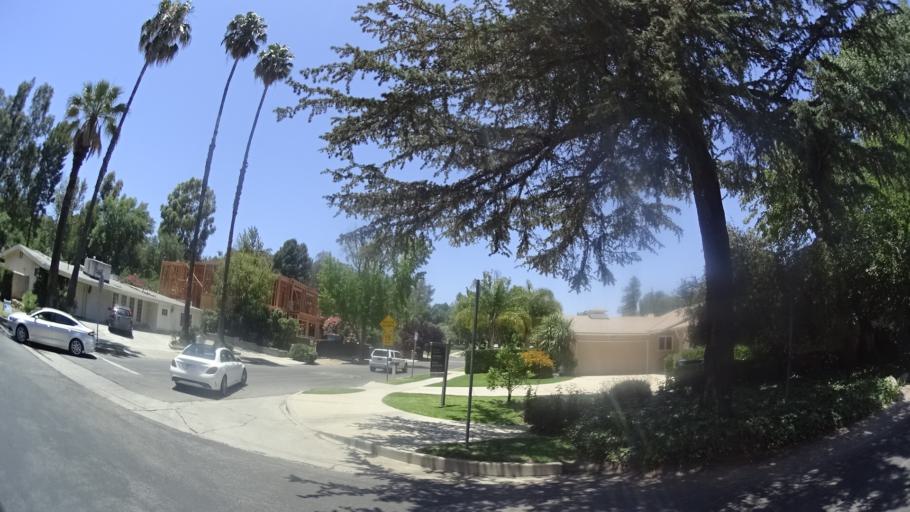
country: US
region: California
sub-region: Los Angeles County
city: Sherman Oaks
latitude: 34.1553
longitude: -118.4837
